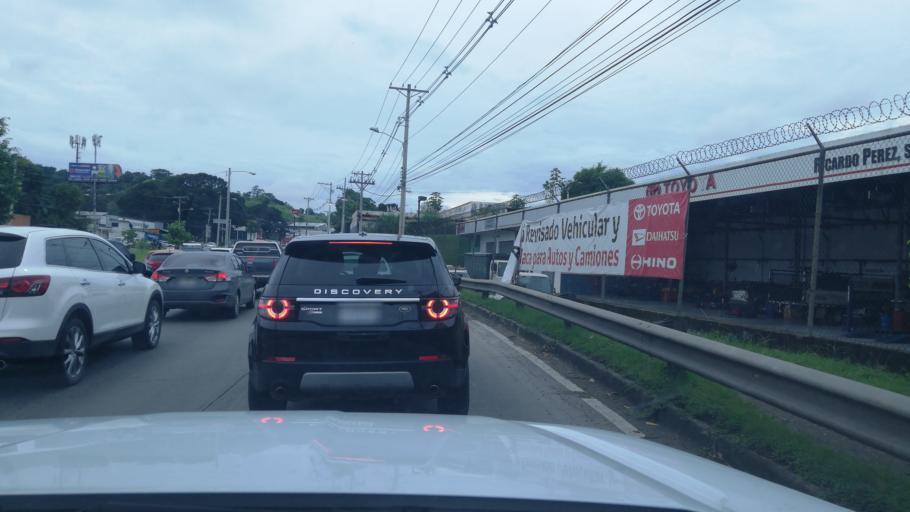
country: PA
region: Panama
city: Las Cumbres
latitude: 9.0708
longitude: -79.5215
